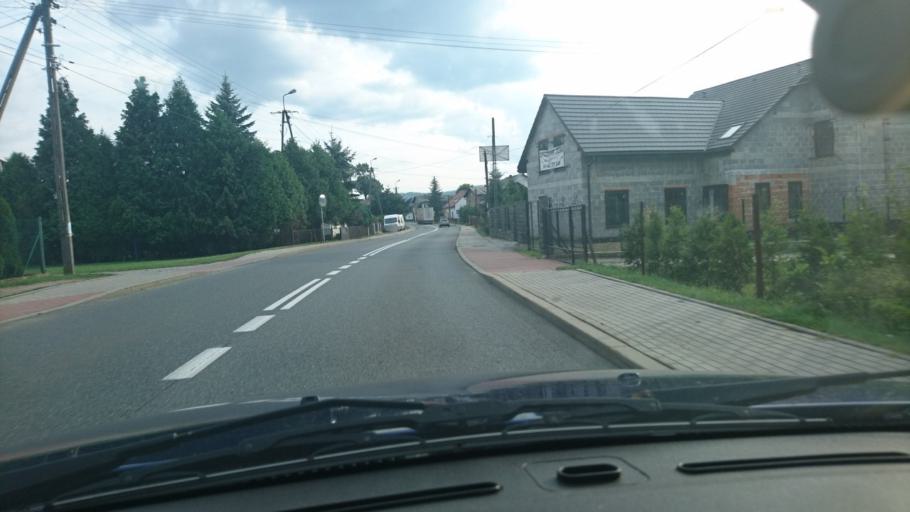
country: PL
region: Silesian Voivodeship
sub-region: Powiat zywiecki
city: Cisiec
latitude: 49.5893
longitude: 19.1049
